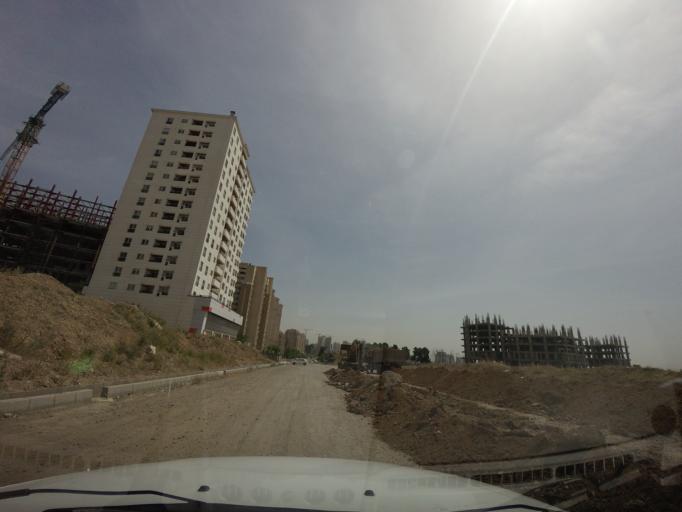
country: IR
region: Tehran
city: Shahr-e Qods
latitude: 35.7525
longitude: 51.1962
